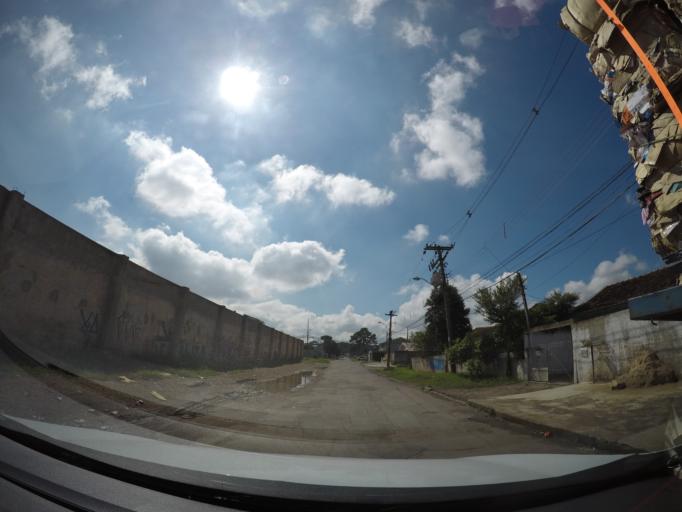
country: BR
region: Parana
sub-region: Sao Jose Dos Pinhais
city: Sao Jose dos Pinhais
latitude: -25.4984
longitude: -49.2207
